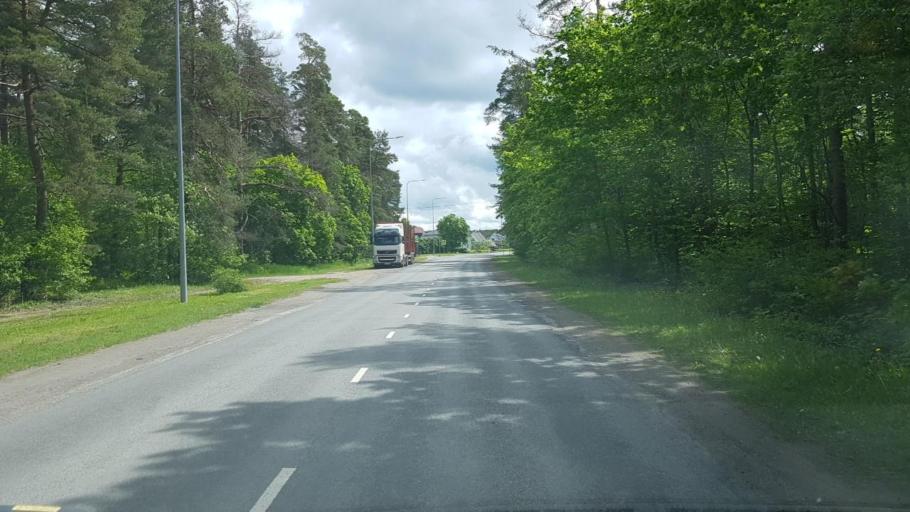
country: EE
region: Laeaene
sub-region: Haapsalu linn
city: Haapsalu
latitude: 58.9287
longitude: 23.5360
